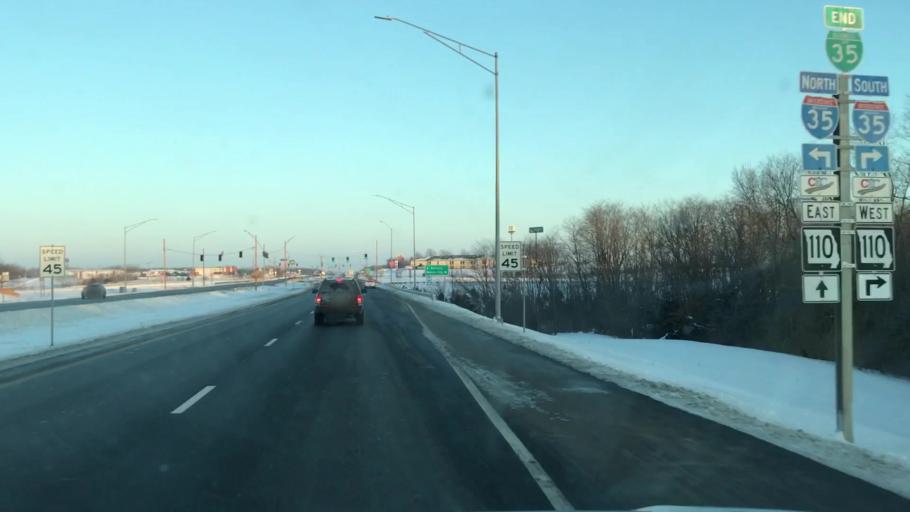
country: US
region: Missouri
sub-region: Clinton County
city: Cameron
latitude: 39.7538
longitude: -94.2236
